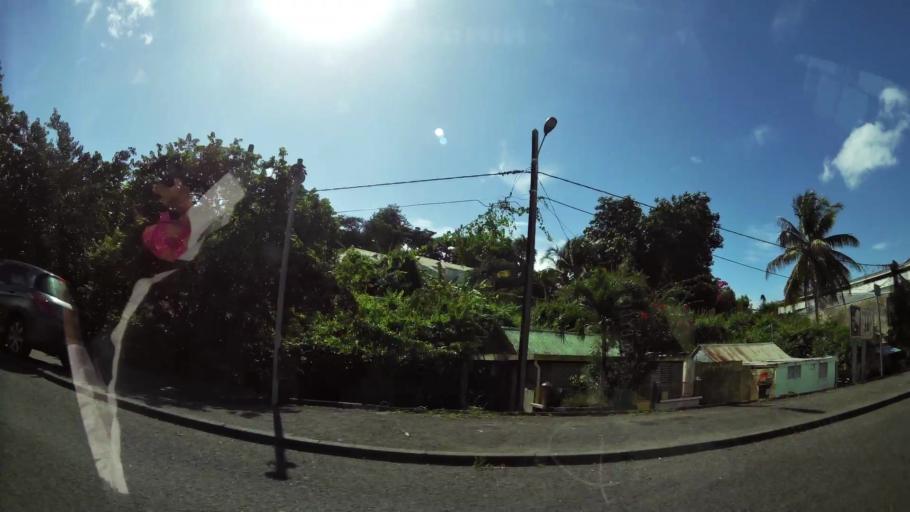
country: GP
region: Guadeloupe
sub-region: Guadeloupe
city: Pointe-a-Pitre
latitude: 16.2385
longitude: -61.5290
